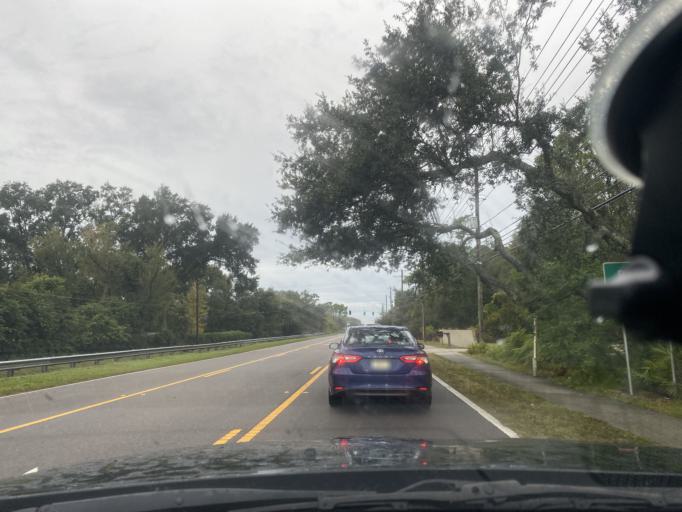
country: US
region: Florida
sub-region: Orange County
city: Azalea Park
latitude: 28.5393
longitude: -81.2697
